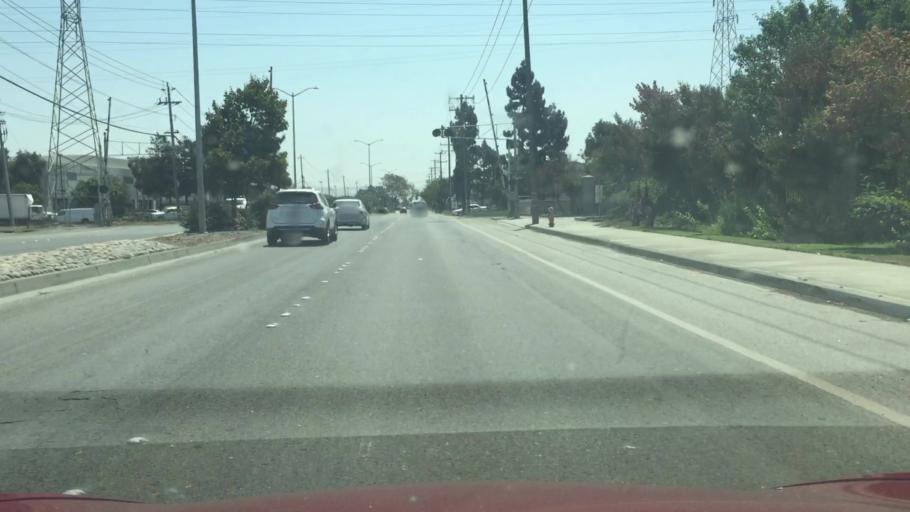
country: US
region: California
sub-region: Alameda County
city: Fremont
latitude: 37.5097
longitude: -121.9893
